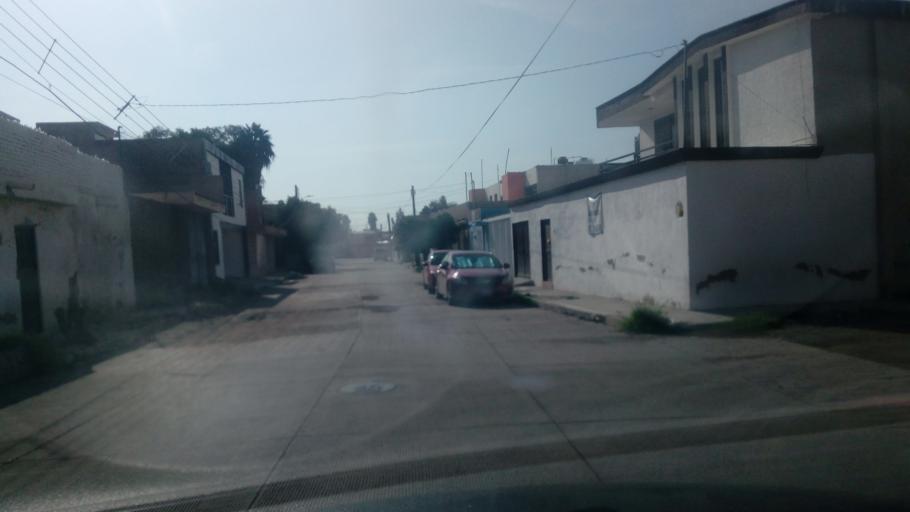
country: MX
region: Durango
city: Victoria de Durango
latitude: 24.0189
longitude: -104.6605
